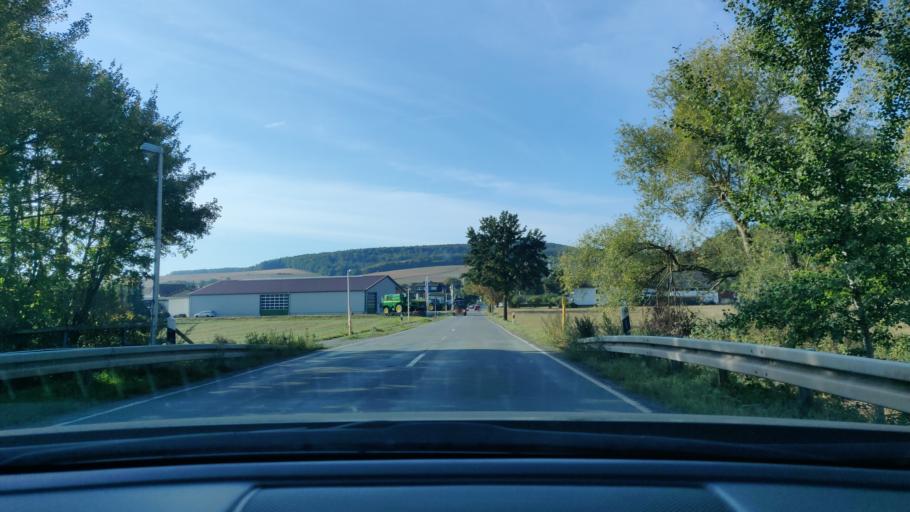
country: DE
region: Hesse
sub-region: Regierungsbezirk Kassel
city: Bad Wildungen
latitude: 51.1361
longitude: 9.1768
